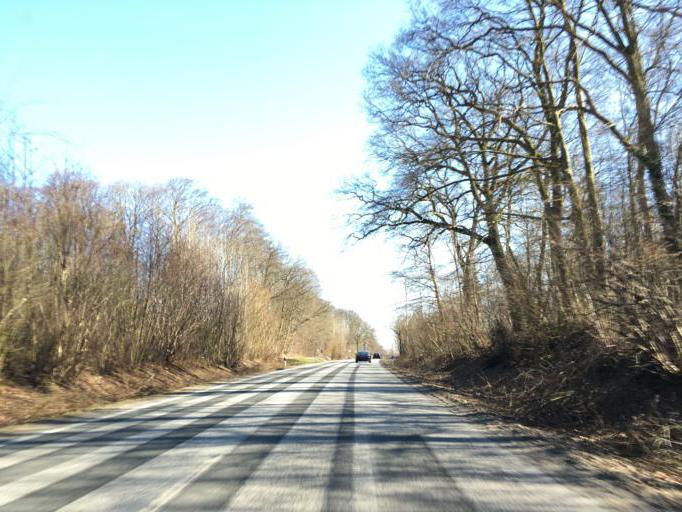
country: DE
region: Schleswig-Holstein
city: Kulpin
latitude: 53.7224
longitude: 10.6748
